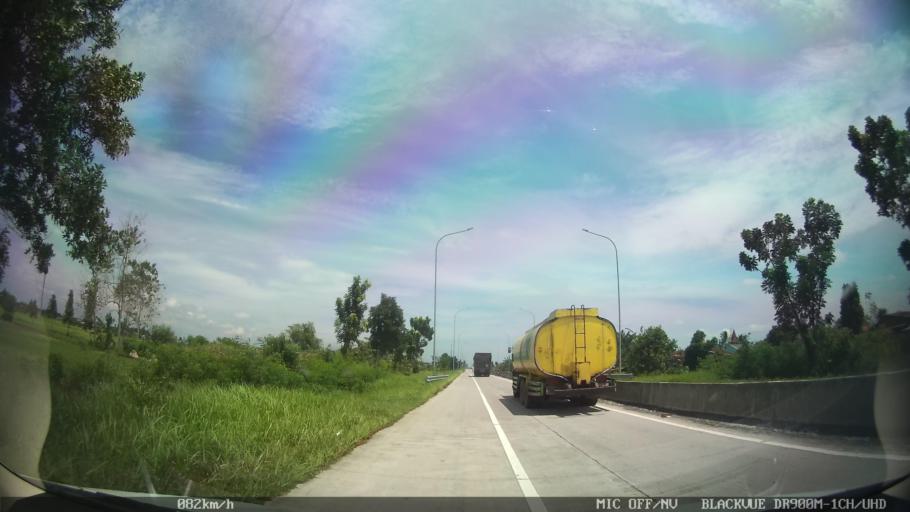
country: ID
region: North Sumatra
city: Perbaungan
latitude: 3.5494
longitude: 98.8887
